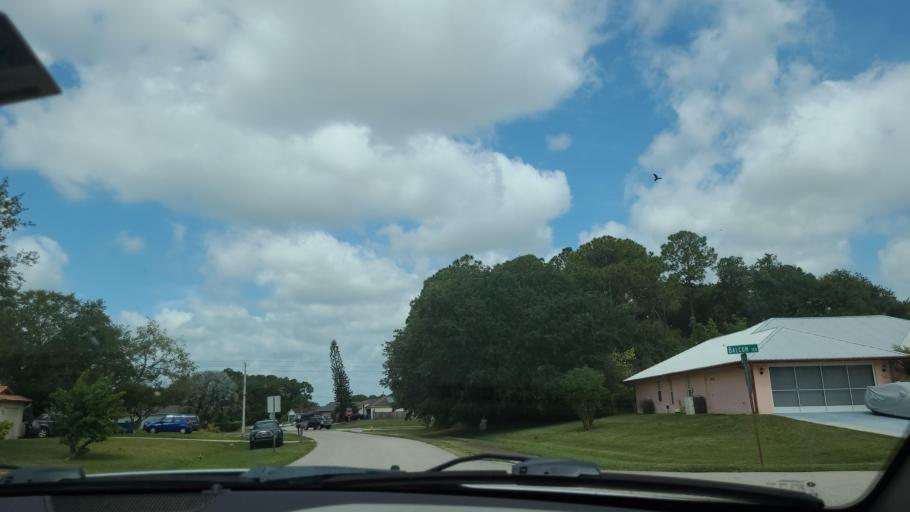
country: US
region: Florida
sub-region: Brevard County
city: Grant-Valkaria
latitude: 27.9676
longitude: -80.6598
